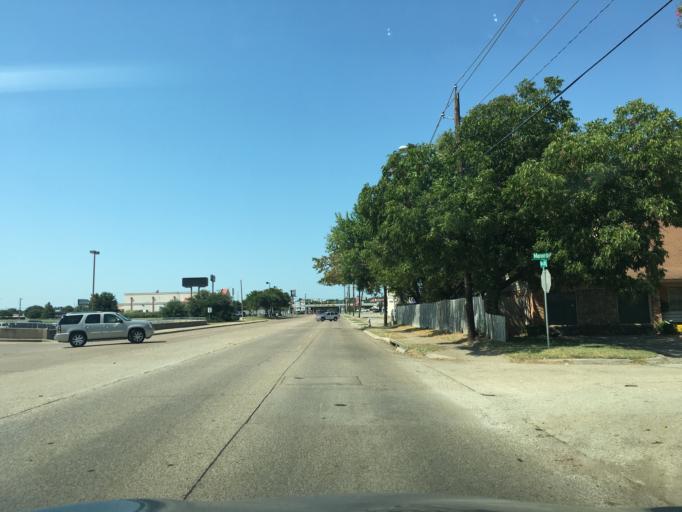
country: US
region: Texas
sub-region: Tarrant County
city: Forest Hill
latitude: 32.6576
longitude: -97.2698
